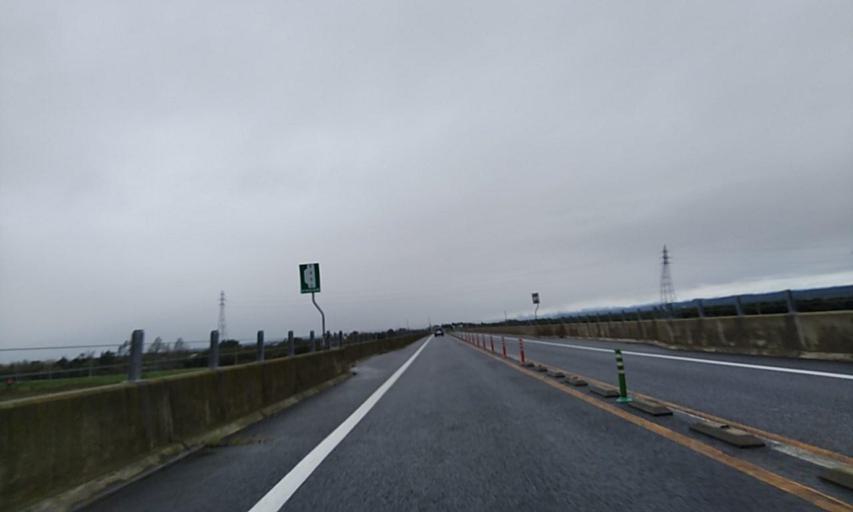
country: JP
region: Hokkaido
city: Kushiro
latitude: 43.0331
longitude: 144.3808
